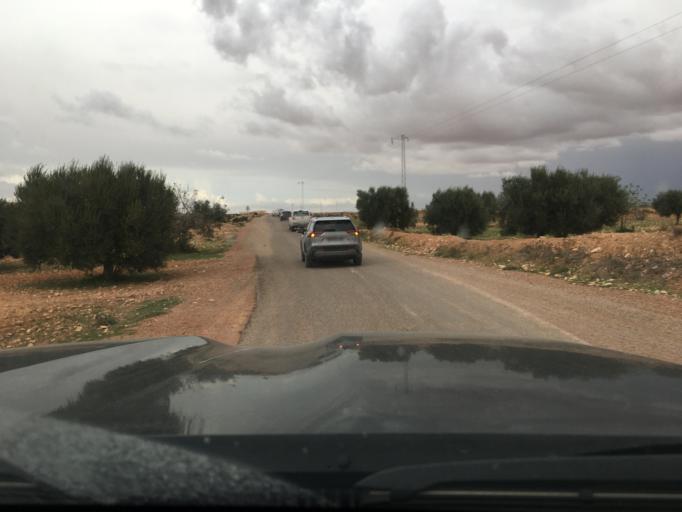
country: TN
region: Madanin
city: Medenine
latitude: 33.2879
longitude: 10.6041
